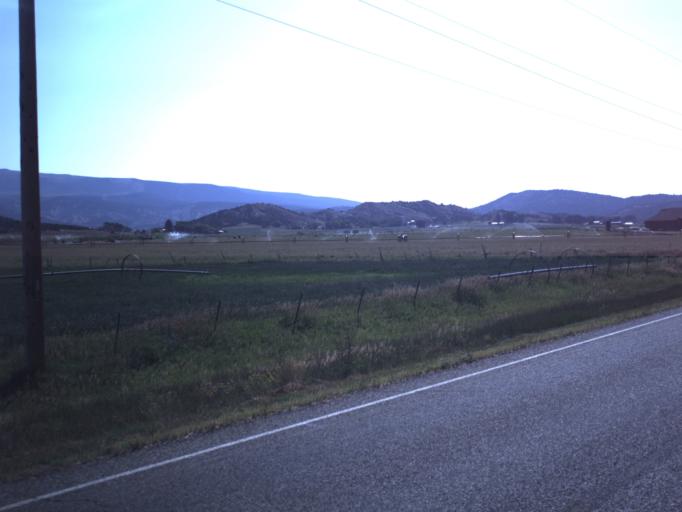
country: US
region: Utah
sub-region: Duchesne County
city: Duchesne
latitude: 40.3783
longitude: -110.7350
